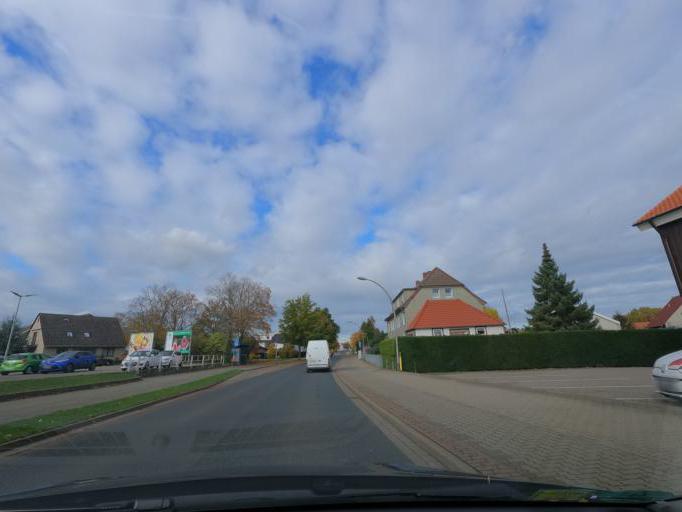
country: DE
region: Lower Saxony
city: Leiferde
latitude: 52.1888
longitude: 10.4815
